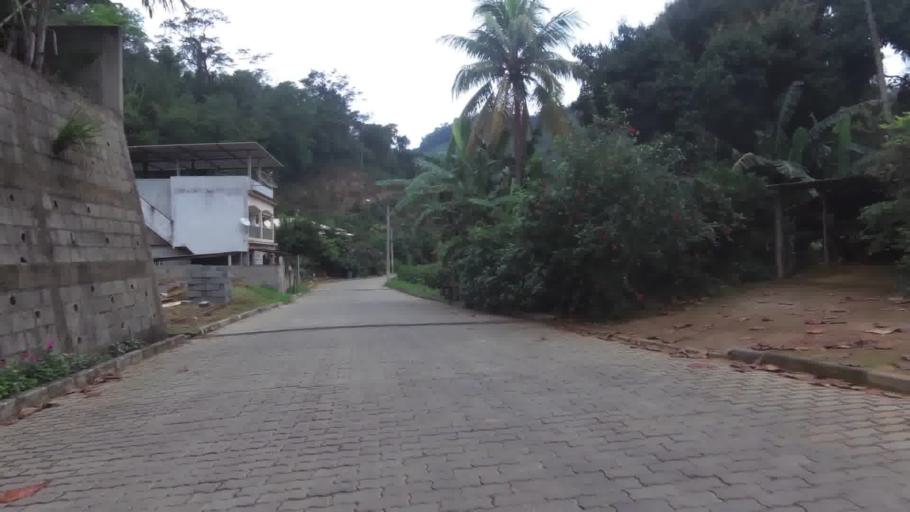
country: BR
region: Espirito Santo
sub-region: Iconha
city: Iconha
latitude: -20.7804
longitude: -40.8270
